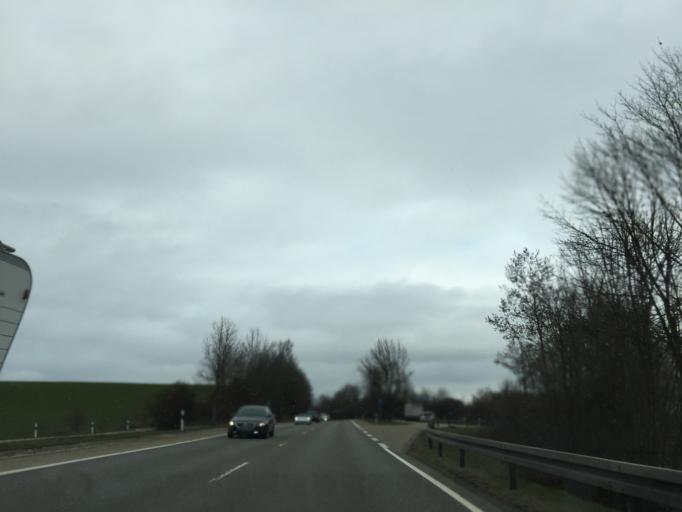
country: DE
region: Baden-Wuerttemberg
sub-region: Freiburg Region
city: Villingen-Schwenningen
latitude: 48.0417
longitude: 8.4892
